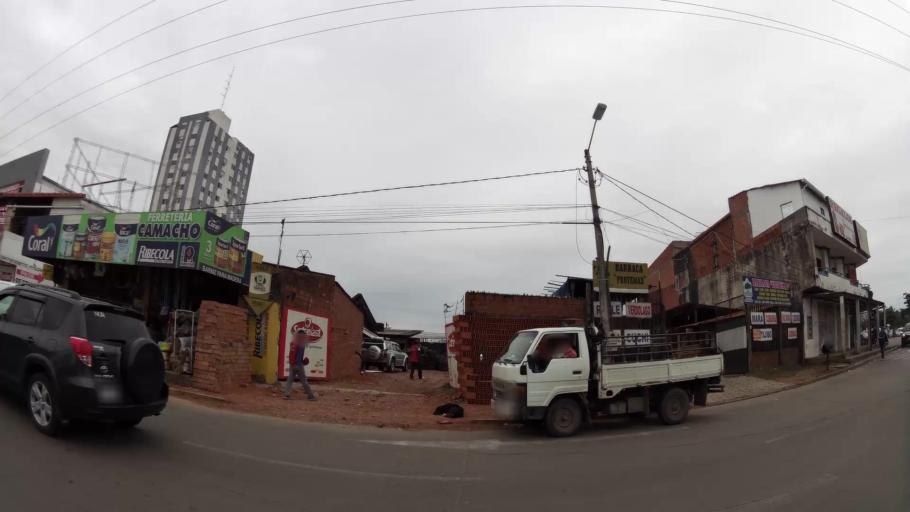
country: BO
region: Santa Cruz
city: Santa Cruz de la Sierra
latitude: -17.8230
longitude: -63.1837
